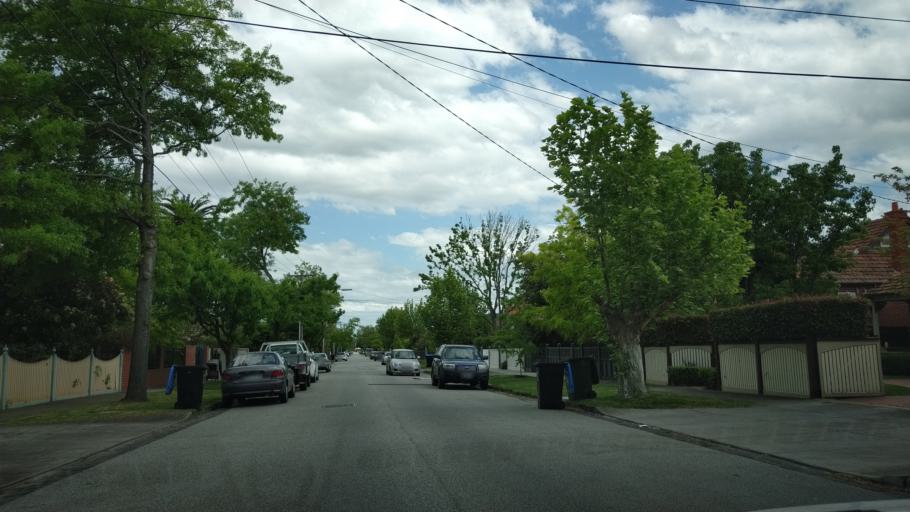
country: AU
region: Victoria
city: Glen Huntly
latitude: -37.8782
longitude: 145.0554
